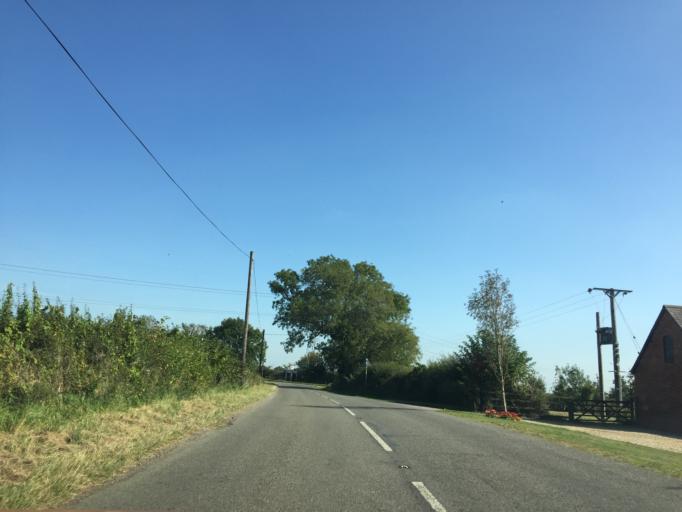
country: GB
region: England
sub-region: Leicestershire
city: Houghton on the Hill
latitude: 52.6409
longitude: -0.9151
